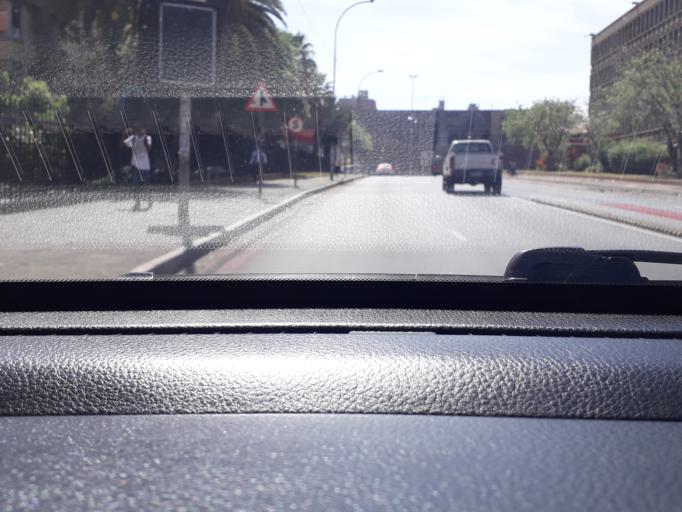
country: ZA
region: Gauteng
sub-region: City of Johannesburg Metropolitan Municipality
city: Johannesburg
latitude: -26.1899
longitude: 28.0399
